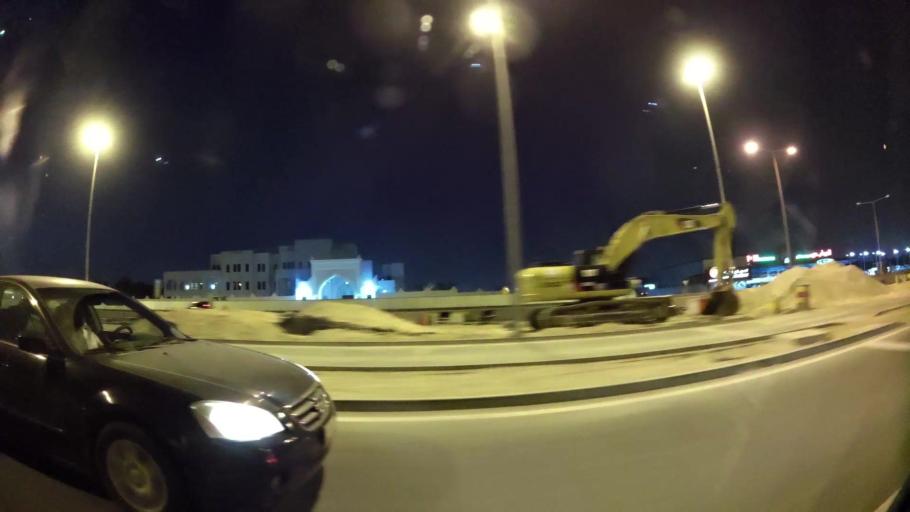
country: QA
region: Baladiyat ar Rayyan
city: Ar Rayyan
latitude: 25.2983
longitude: 51.4380
